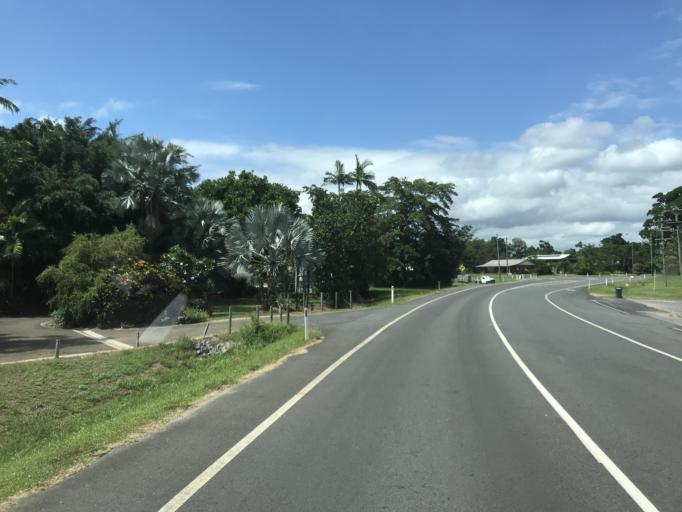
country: AU
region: Queensland
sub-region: Cassowary Coast
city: Innisfail
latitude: -17.8702
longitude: 146.1059
